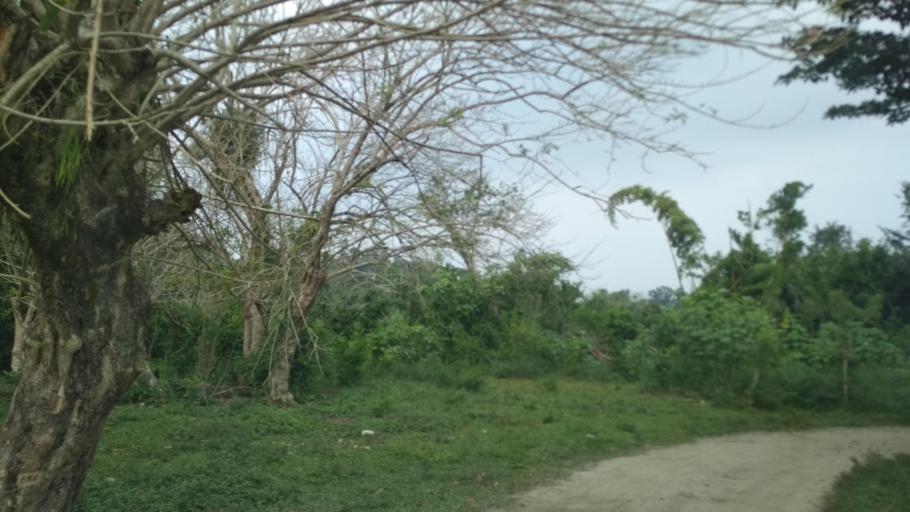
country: MM
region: Kayah
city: Loikaw
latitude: 20.2180
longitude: 97.3354
